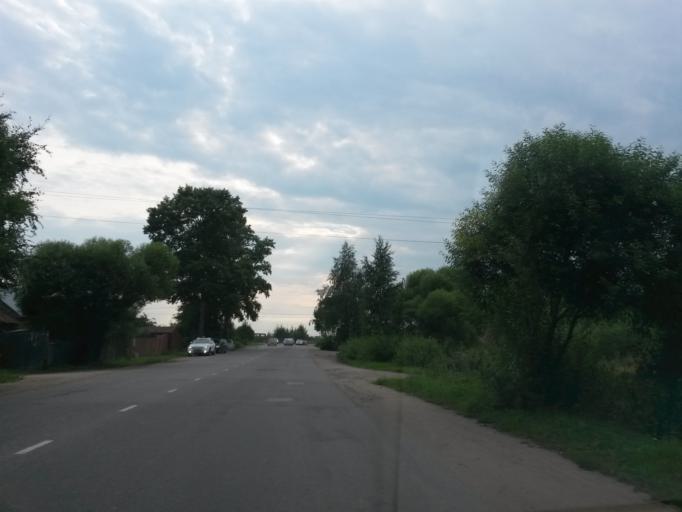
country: RU
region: Jaroslavl
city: Yaroslavl
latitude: 57.6036
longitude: 39.7989
